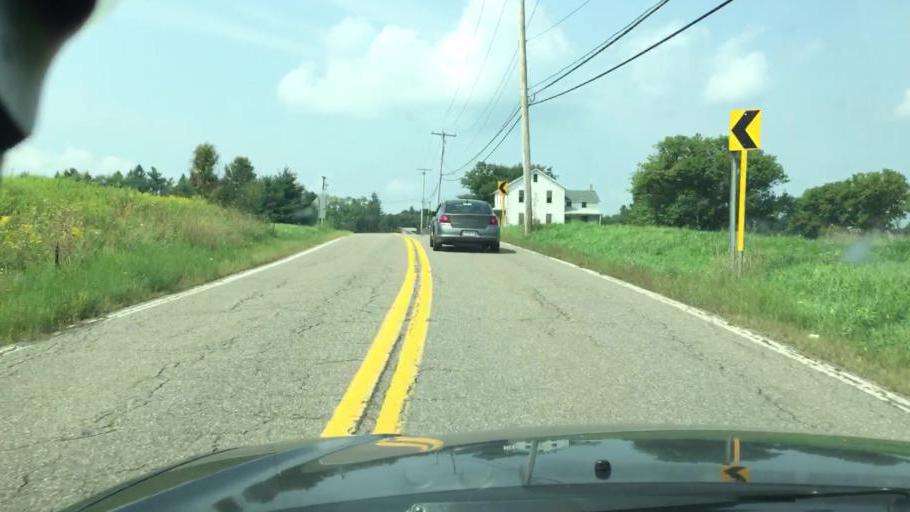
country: US
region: Pennsylvania
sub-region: Luzerne County
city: Harleigh
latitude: 41.0091
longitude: -75.9993
